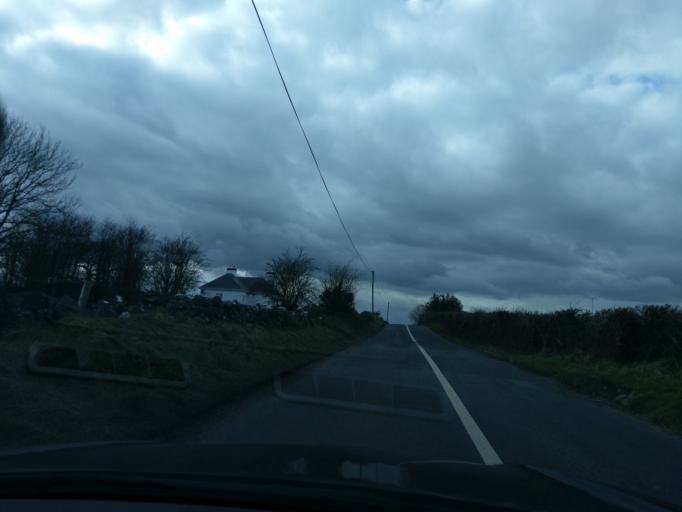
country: IE
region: Connaught
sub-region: County Galway
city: Athenry
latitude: 53.4885
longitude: -8.5851
